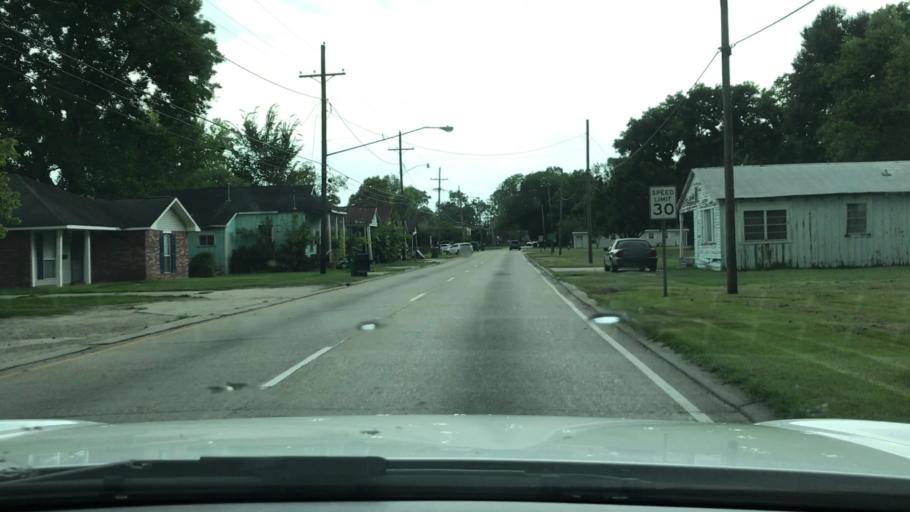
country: US
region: Louisiana
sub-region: Iberville Parish
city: Plaquemine
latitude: 30.2838
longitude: -91.2284
